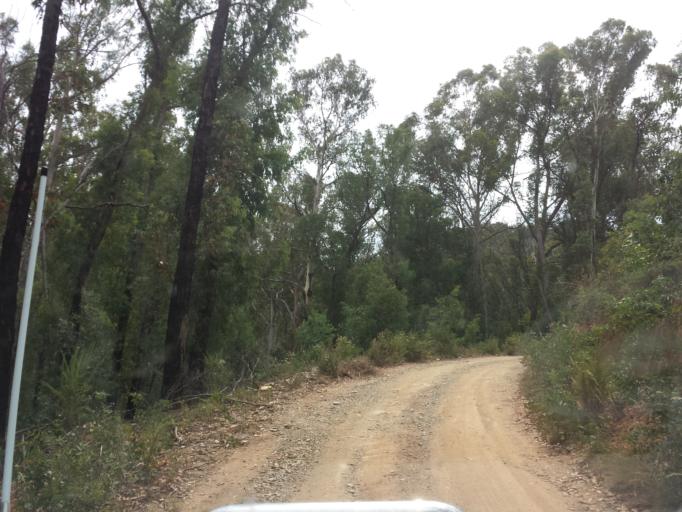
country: AU
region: Victoria
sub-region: Wellington
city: Heyfield
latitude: -37.7542
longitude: 146.4940
